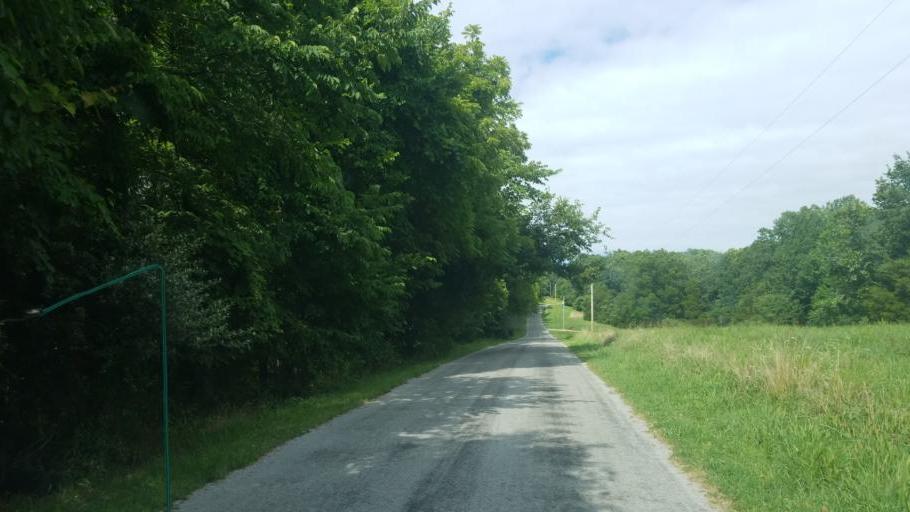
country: US
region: Illinois
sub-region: Union County
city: Cobden
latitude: 37.6076
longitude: -89.3617
